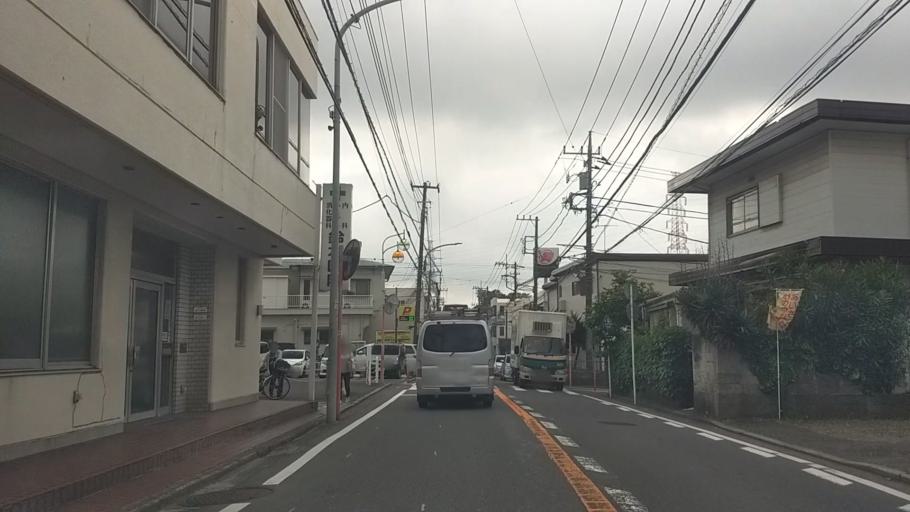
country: JP
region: Kanagawa
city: Kamakura
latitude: 35.3814
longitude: 139.5367
